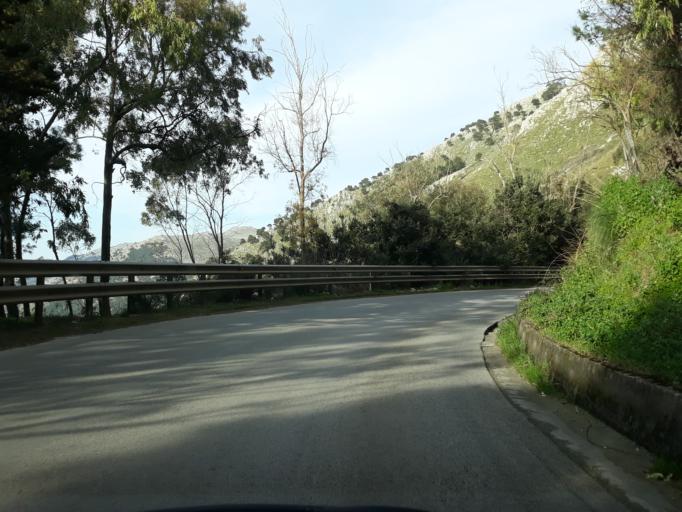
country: IT
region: Sicily
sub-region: Palermo
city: Torretta
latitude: 38.1123
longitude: 13.2391
